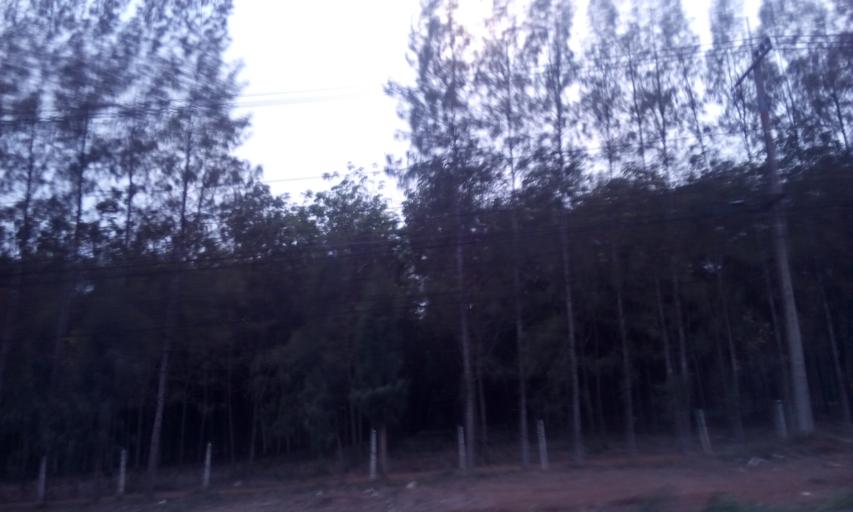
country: TH
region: Chachoengsao
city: Plaeng Yao
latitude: 13.5198
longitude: 101.2659
